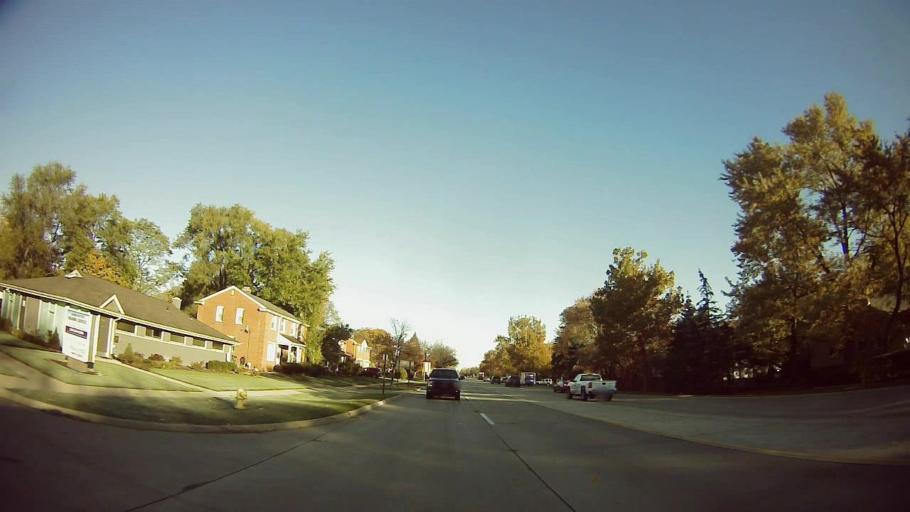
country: US
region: Michigan
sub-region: Oakland County
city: Huntington Woods
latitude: 42.4761
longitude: -83.1828
